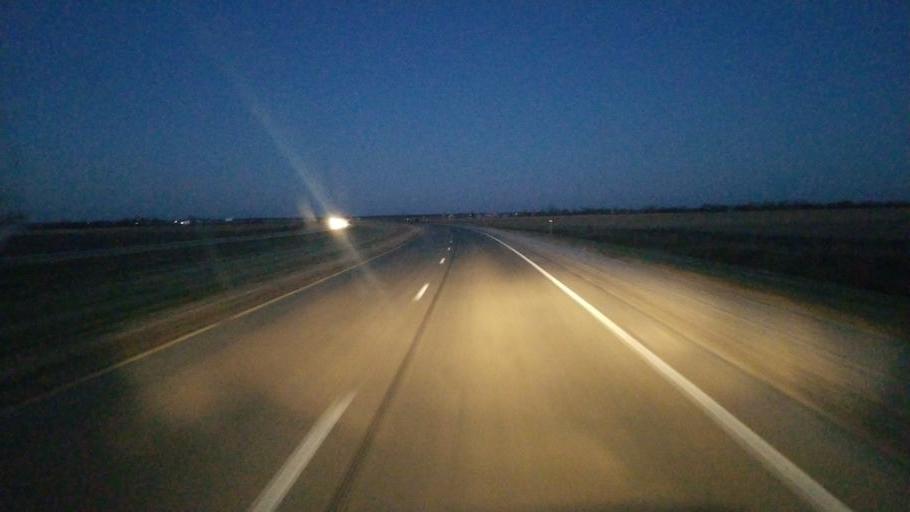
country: US
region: Iowa
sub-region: Des Moines County
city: West Burlington
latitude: 40.8346
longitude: -91.2943
